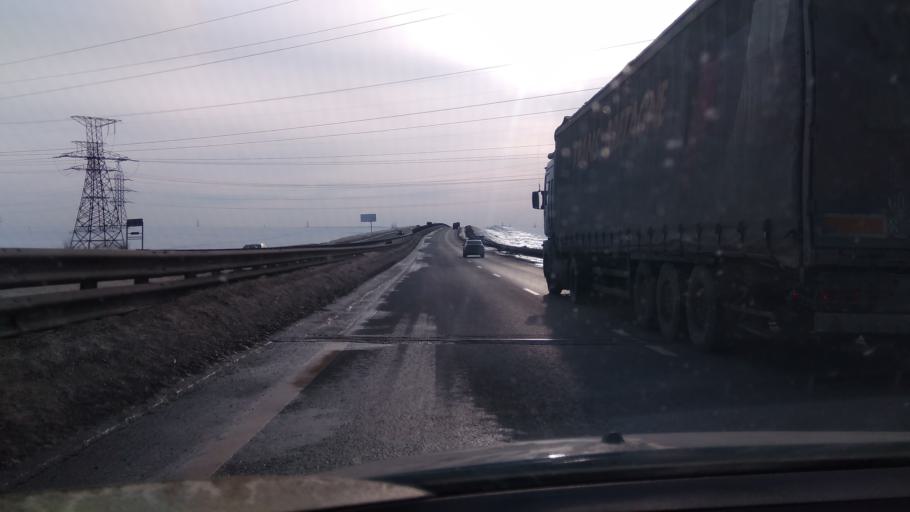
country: RU
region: Perm
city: Ferma
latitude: 57.9385
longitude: 56.3673
